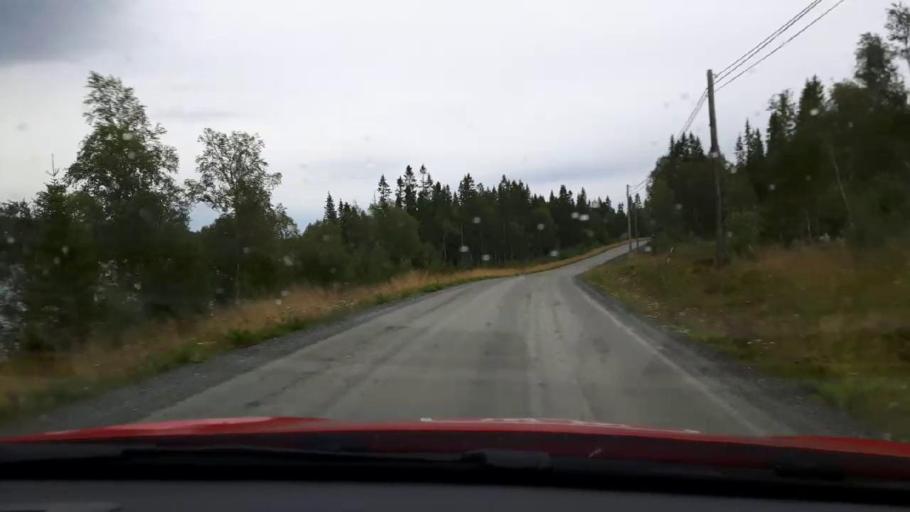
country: SE
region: Jaemtland
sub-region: Are Kommun
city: Are
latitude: 63.4845
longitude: 13.1449
